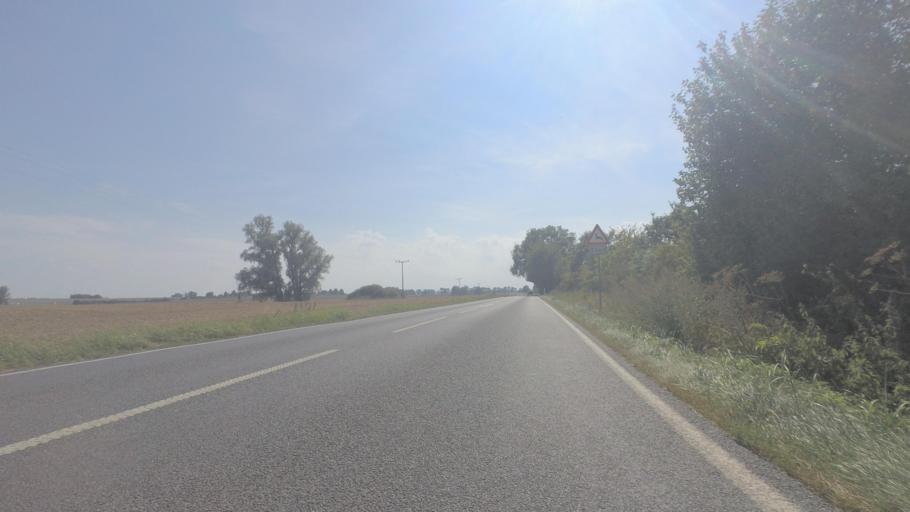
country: DE
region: Mecklenburg-Vorpommern
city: Brandshagen
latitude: 54.1605
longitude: 13.1678
